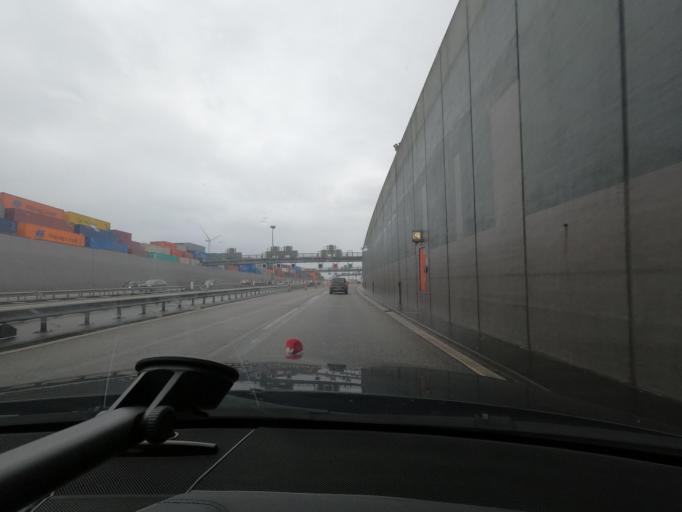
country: DE
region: Hamburg
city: Duvenstedt
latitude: 53.7179
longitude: 10.1096
